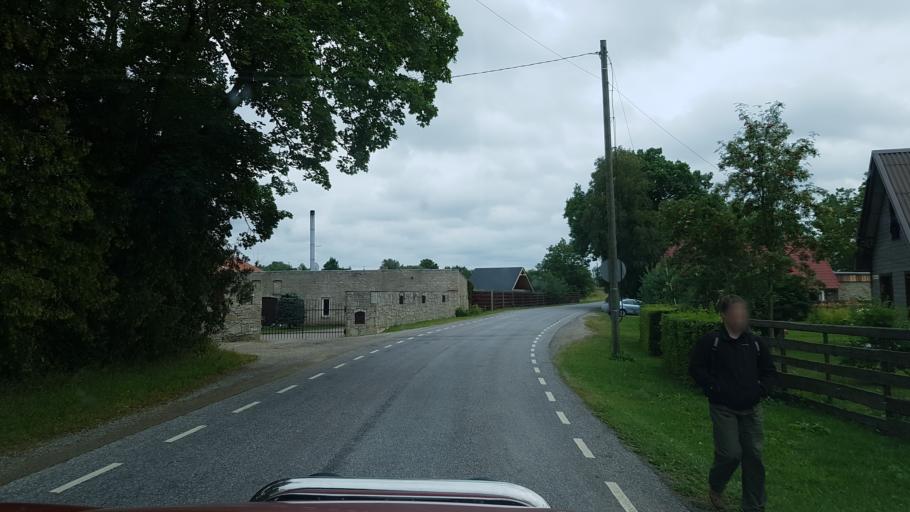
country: EE
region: Ida-Virumaa
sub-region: Puessi linn
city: Pussi
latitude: 59.3788
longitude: 27.0382
